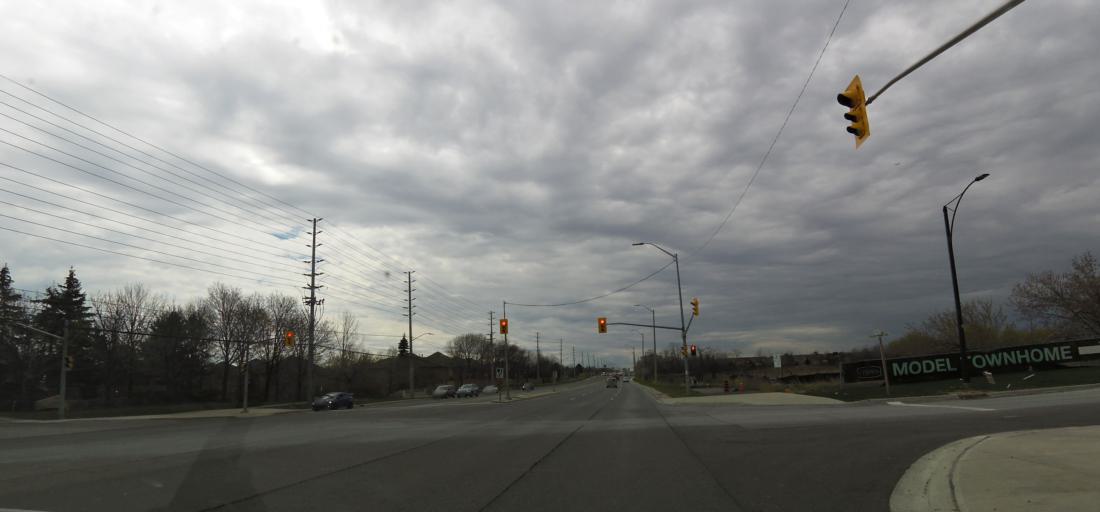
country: CA
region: Ontario
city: Mississauga
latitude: 43.6056
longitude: -79.6544
